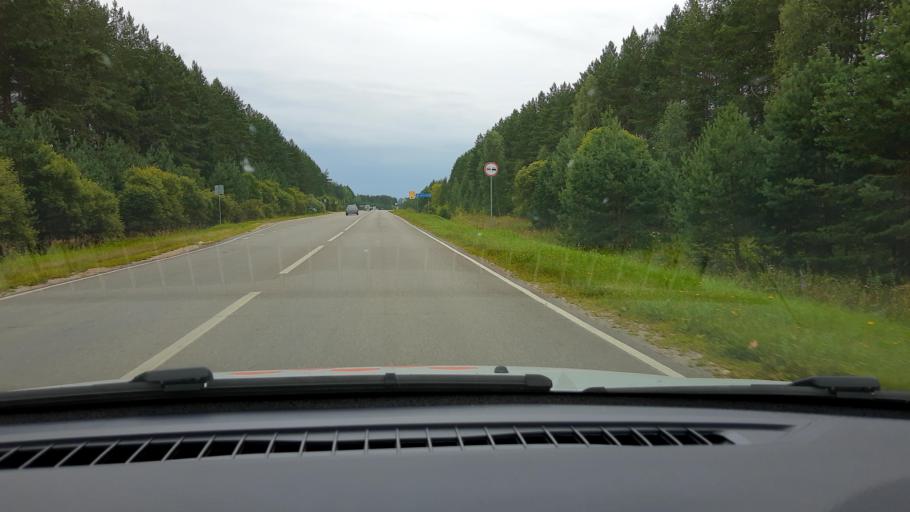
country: RU
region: Nizjnij Novgorod
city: Vyyezdnoye
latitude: 55.1978
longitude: 43.6199
